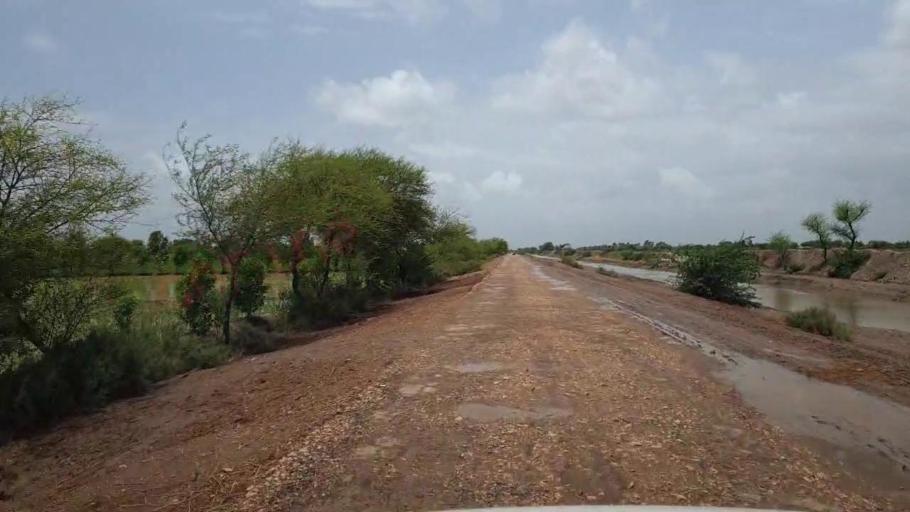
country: PK
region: Sindh
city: Kario
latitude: 24.7120
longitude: 68.5947
